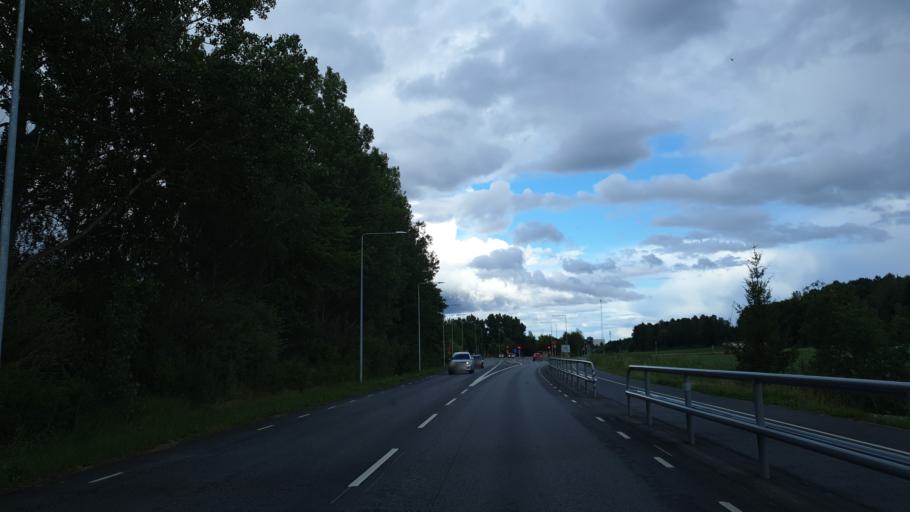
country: SE
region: Stockholm
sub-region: Jarfalla Kommun
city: Jakobsberg
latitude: 59.4204
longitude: 17.8130
